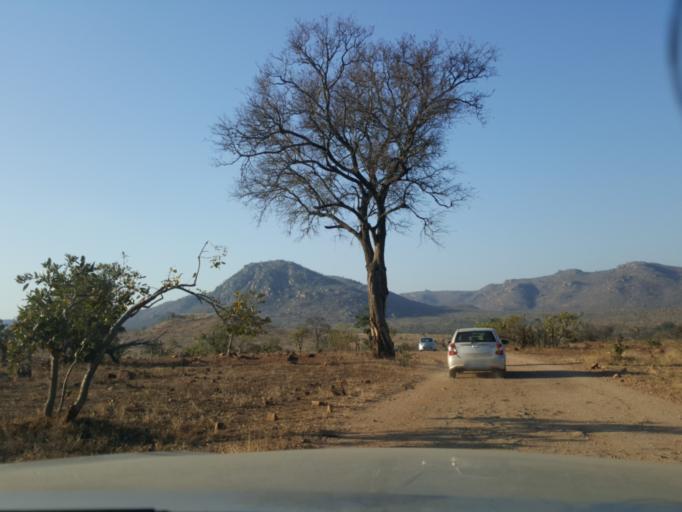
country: SZ
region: Hhohho
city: Ntfonjeni
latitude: -25.4261
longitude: 31.4370
